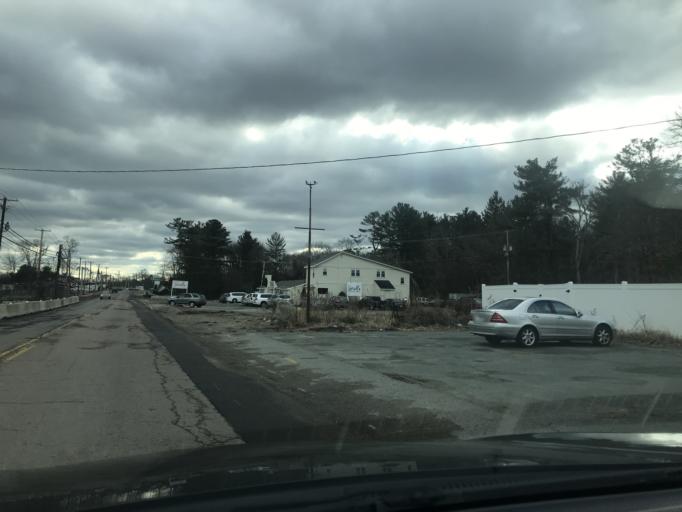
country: US
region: Massachusetts
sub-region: Plymouth County
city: Abington
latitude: 42.1408
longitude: -70.9521
